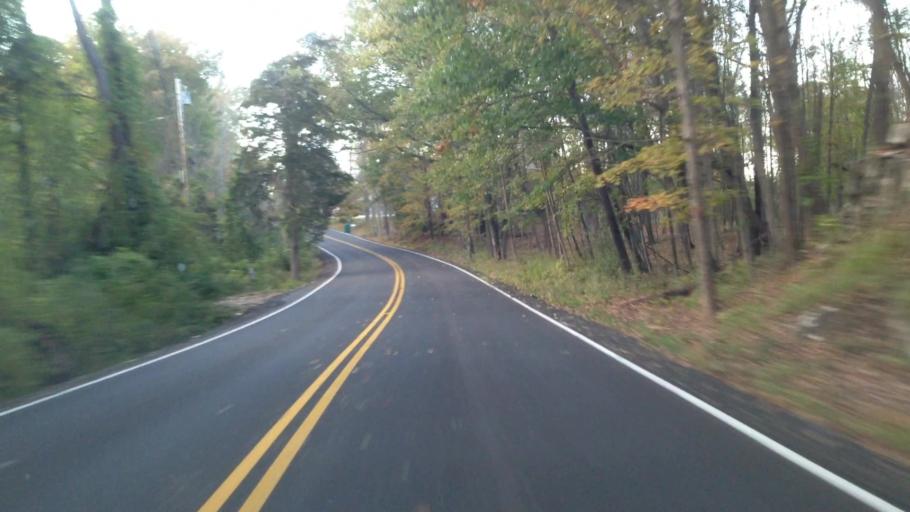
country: US
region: New York
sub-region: Ulster County
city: Tillson
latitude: 41.8227
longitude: -74.0354
